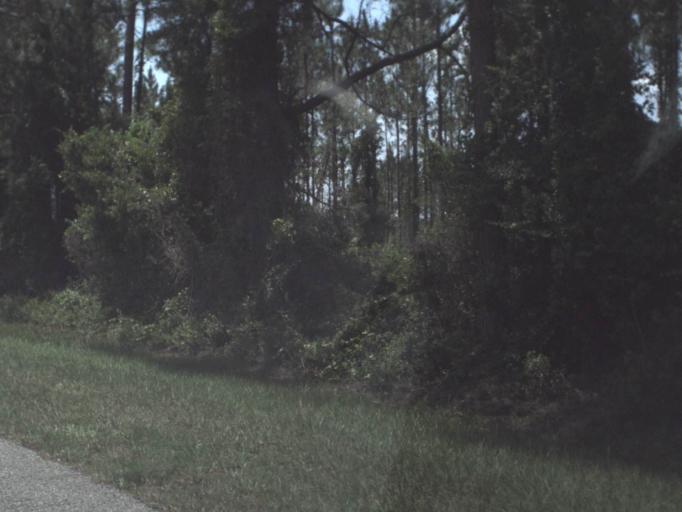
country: US
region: Florida
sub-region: Saint Johns County
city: Butler Beach
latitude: 29.7008
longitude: -81.2981
